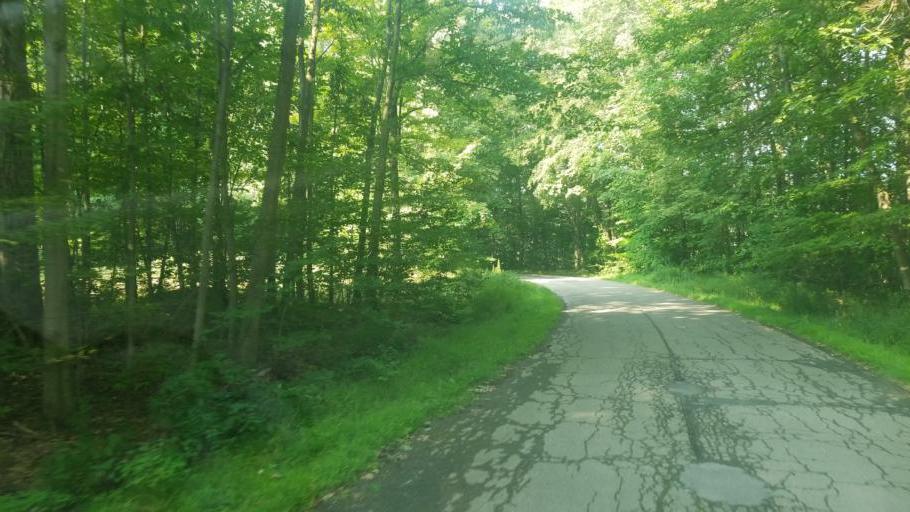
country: US
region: Pennsylvania
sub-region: Crawford County
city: Pymatuning Central
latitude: 41.6397
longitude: -80.4936
